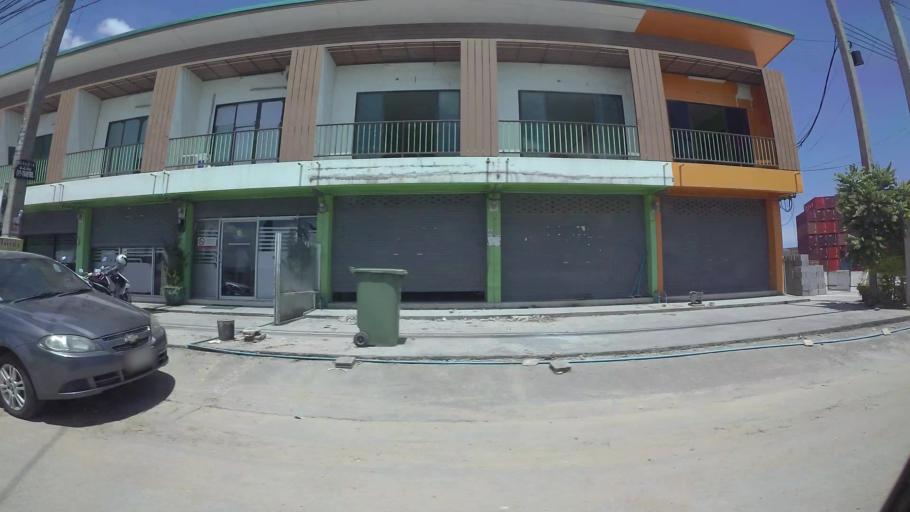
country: TH
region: Chon Buri
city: Si Racha
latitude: 13.1210
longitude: 100.9555
